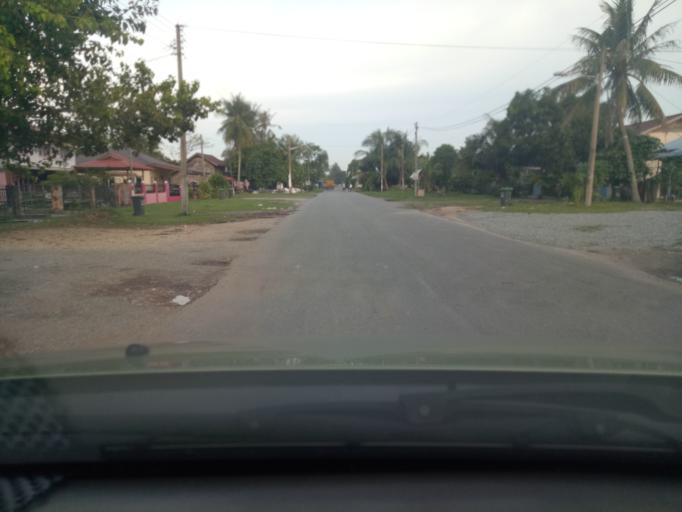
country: MY
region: Kedah
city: Alor Setar
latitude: 6.1222
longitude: 100.3560
